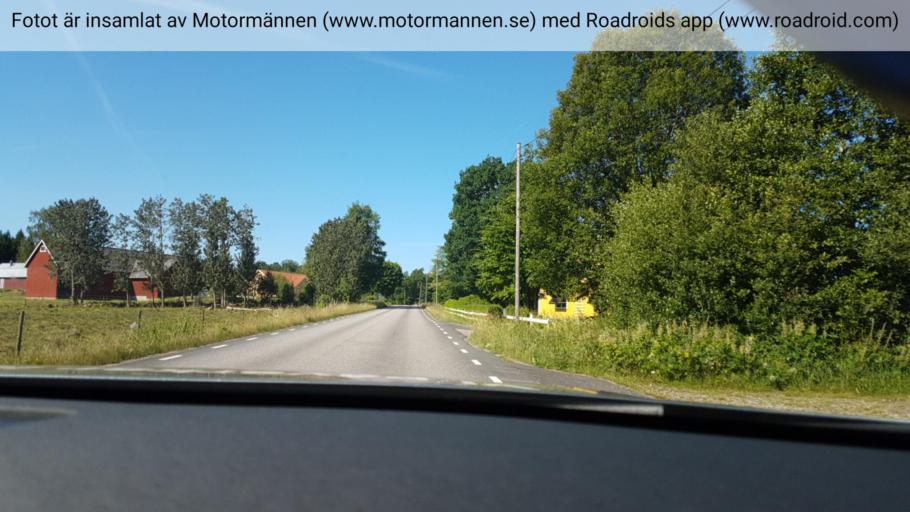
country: SE
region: Vaestra Goetaland
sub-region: Ulricehamns Kommun
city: Ulricehamn
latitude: 57.8553
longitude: 13.3975
